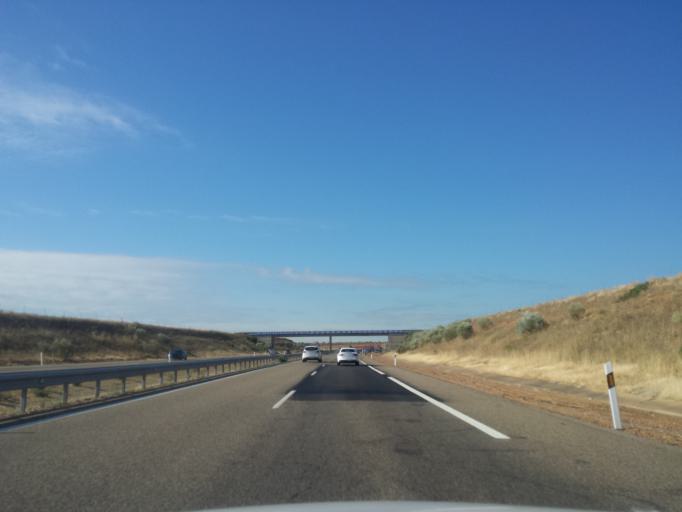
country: ES
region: Castille and Leon
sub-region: Provincia de Leon
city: Villamanan
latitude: 42.3617
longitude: -5.5964
